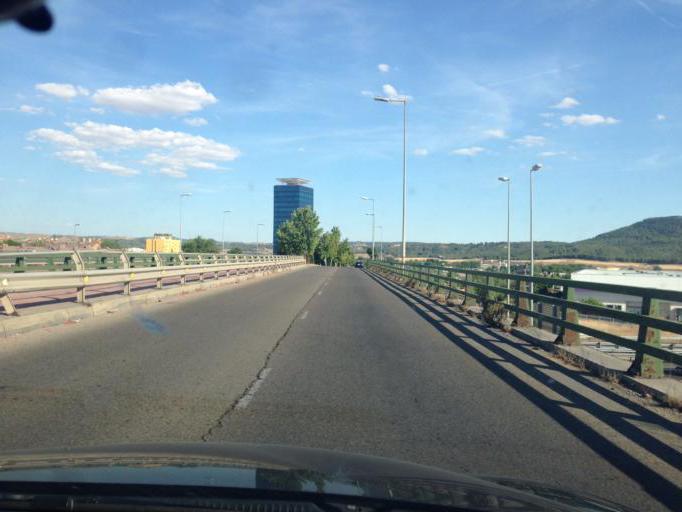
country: ES
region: Madrid
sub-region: Provincia de Madrid
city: Alcala de Henares
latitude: 40.4842
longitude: -3.4003
